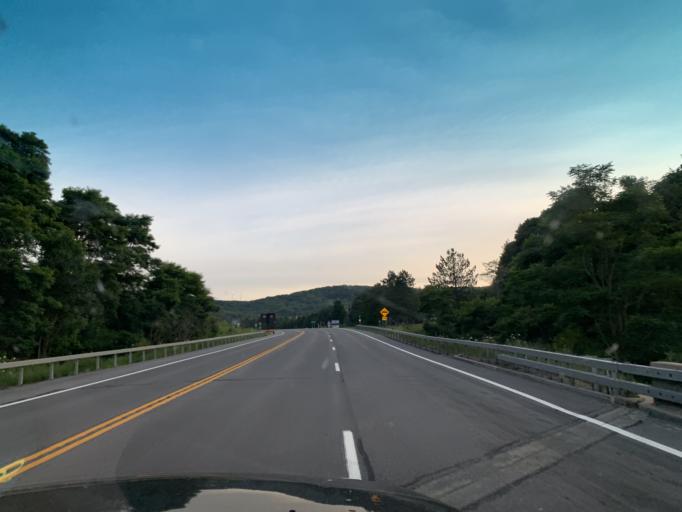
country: US
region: New York
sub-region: Oneida County
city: Chadwicks
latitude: 42.9445
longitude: -75.2497
